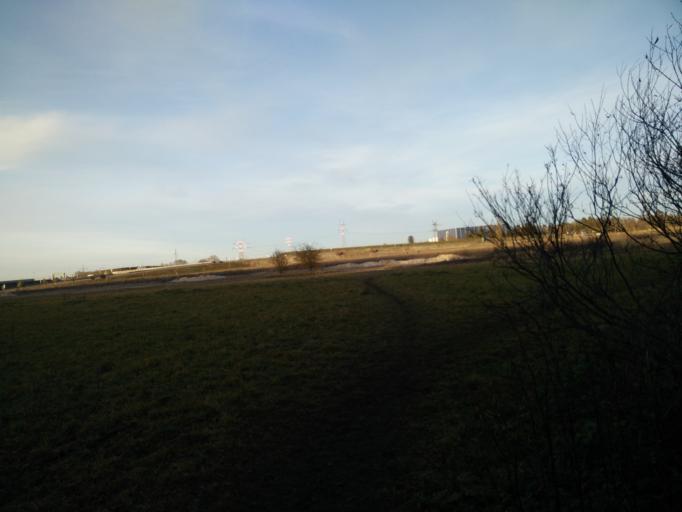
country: DE
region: Bavaria
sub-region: Upper Bavaria
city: Pasing
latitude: 48.1698
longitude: 11.4250
